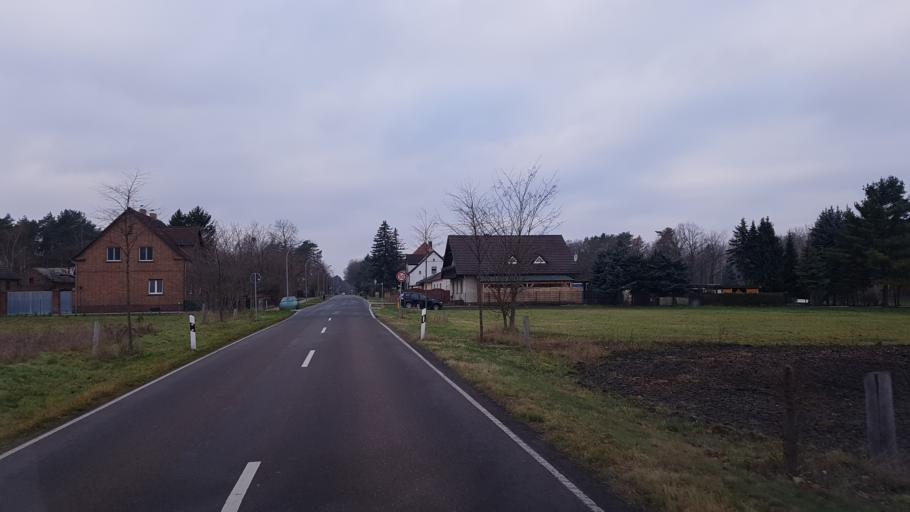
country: DE
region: Brandenburg
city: Sallgast
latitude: 51.5602
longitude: 13.8787
